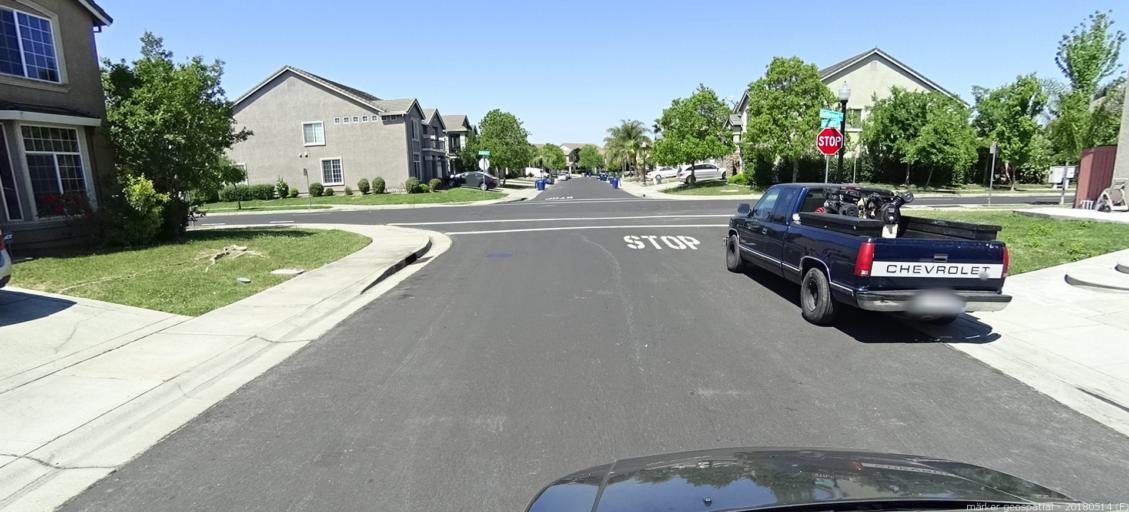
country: US
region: California
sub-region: Yolo County
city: West Sacramento
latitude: 38.6289
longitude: -121.5279
